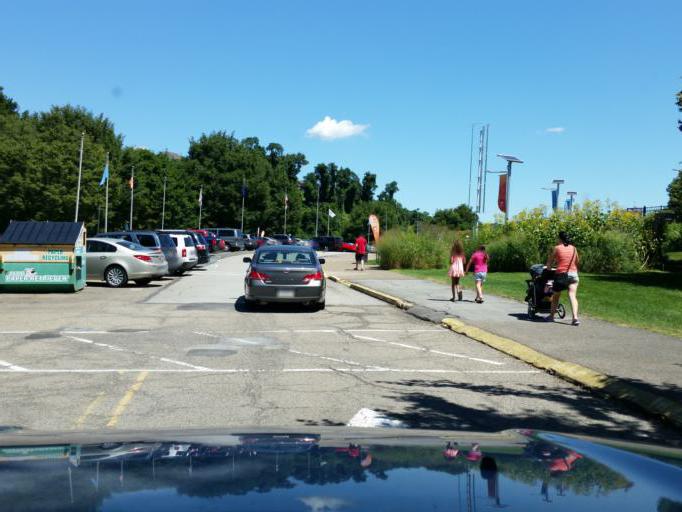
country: US
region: Pennsylvania
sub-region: Allegheny County
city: Sharpsburg
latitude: 40.4839
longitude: -79.9229
